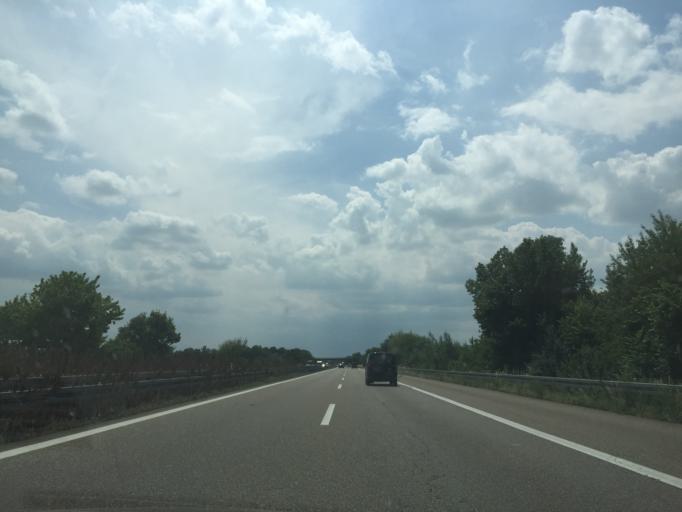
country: DE
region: Baden-Wuerttemberg
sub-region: Karlsruhe Region
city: Schriesheim
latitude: 49.4945
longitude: 8.6391
